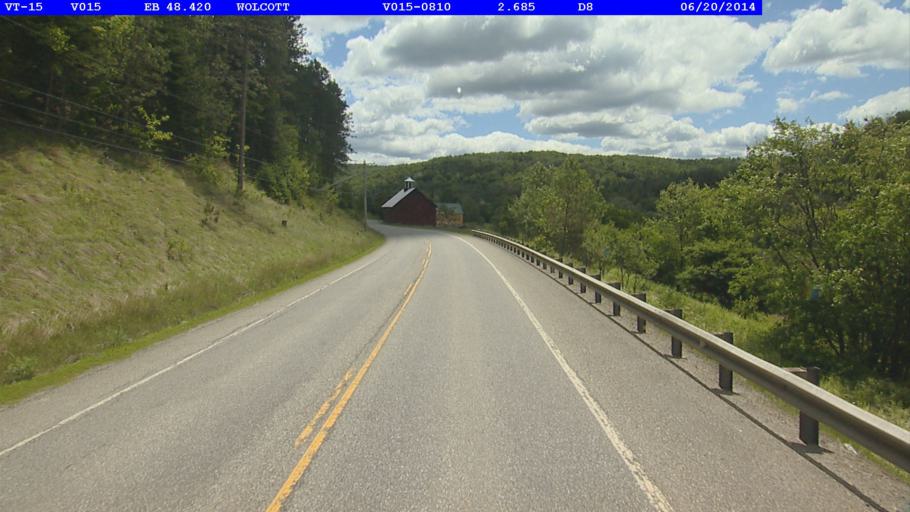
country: US
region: Vermont
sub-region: Lamoille County
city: Morrisville
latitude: 44.5571
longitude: -72.4856
